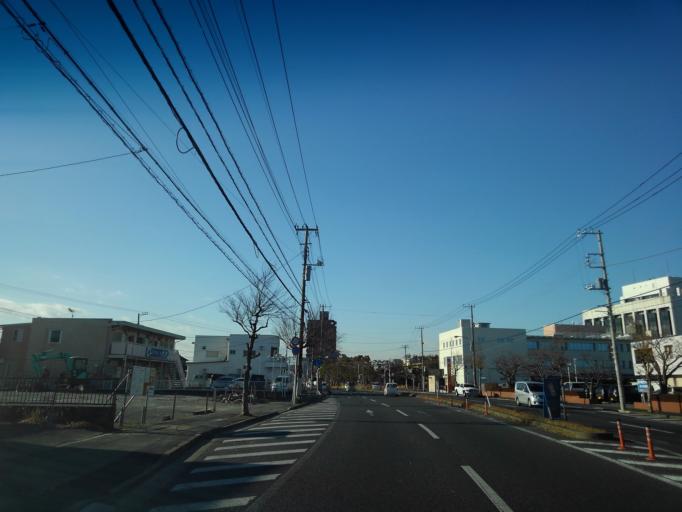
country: JP
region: Chiba
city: Kimitsu
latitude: 35.3283
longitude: 139.9038
